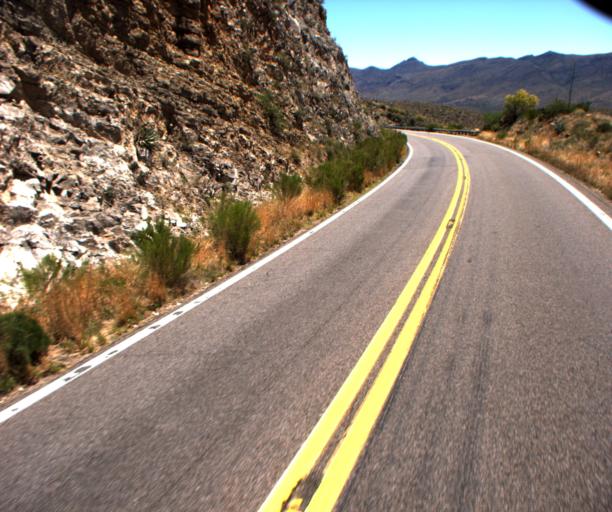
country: US
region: Arizona
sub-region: Pinal County
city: Kearny
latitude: 33.1824
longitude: -110.8116
